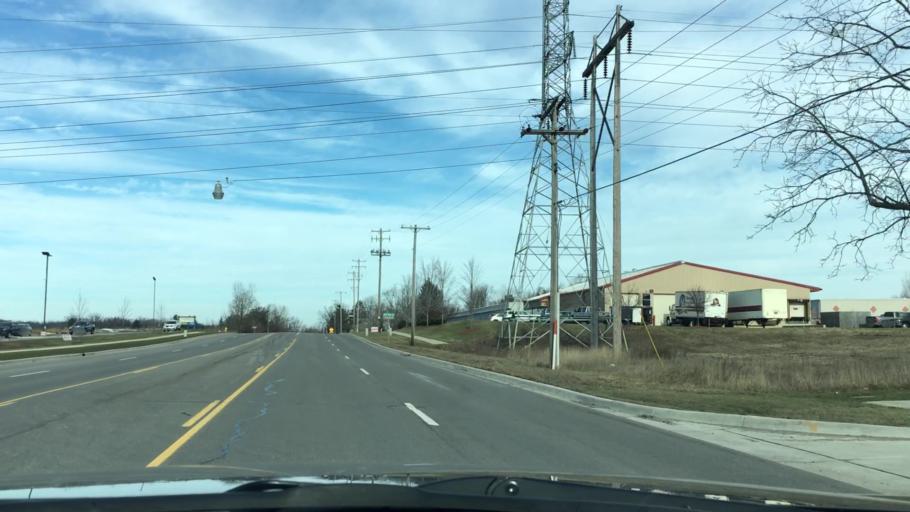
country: US
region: Michigan
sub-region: Kent County
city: Walker
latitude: 43.0249
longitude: -85.7635
